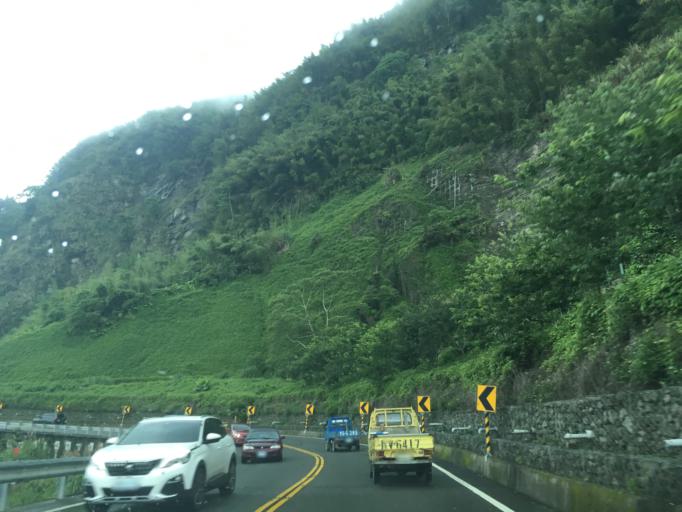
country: TW
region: Taiwan
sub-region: Chiayi
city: Jiayi Shi
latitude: 23.4524
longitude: 120.6768
